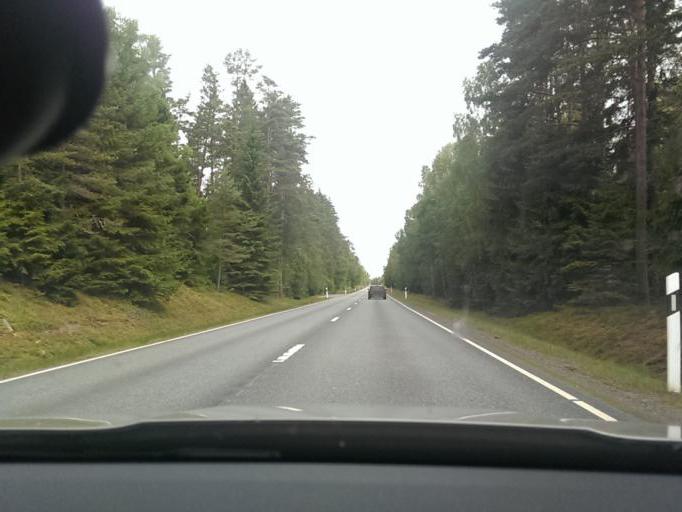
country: SE
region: Joenkoeping
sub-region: Varnamo Kommun
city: Varnamo
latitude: 57.2707
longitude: 13.9703
